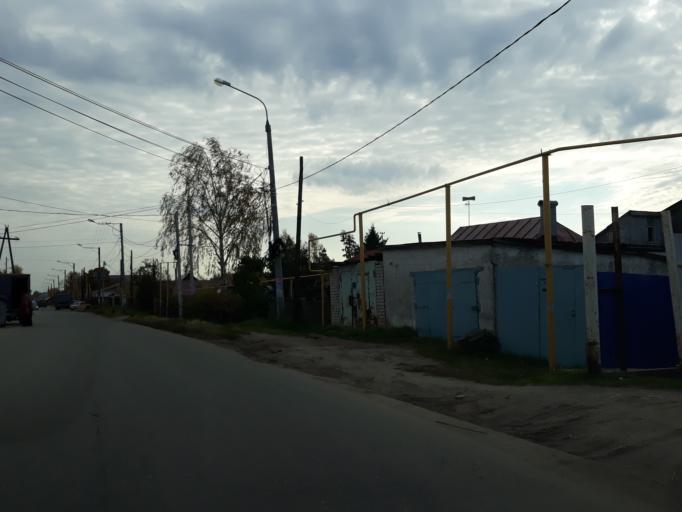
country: RU
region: Nizjnij Novgorod
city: Nizhniy Novgorod
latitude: 56.2356
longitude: 43.9944
